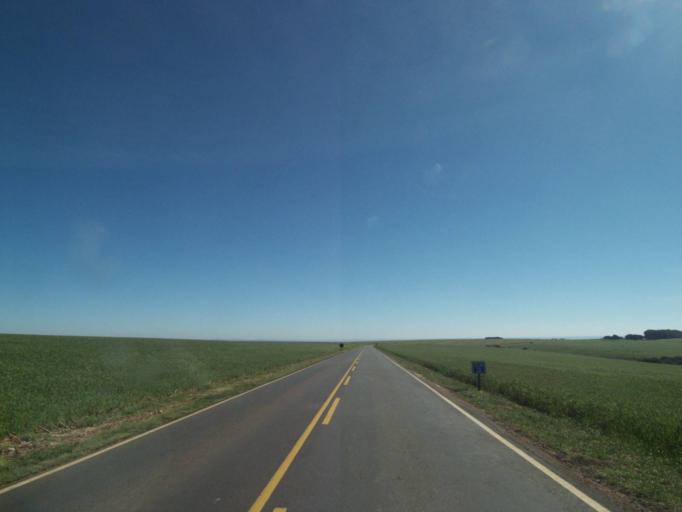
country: BR
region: Parana
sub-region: Tibagi
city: Tibagi
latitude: -24.5679
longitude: -50.2853
